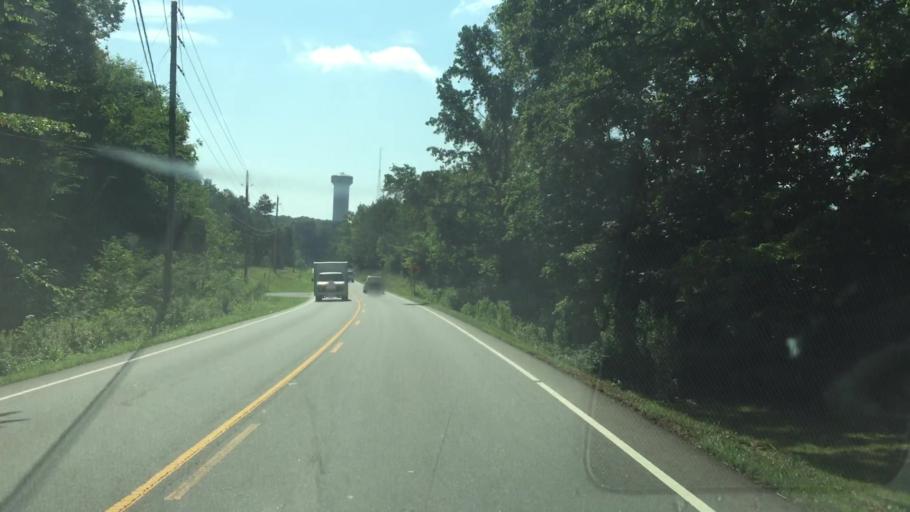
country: US
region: North Carolina
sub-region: Mecklenburg County
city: Mint Hill
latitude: 35.1660
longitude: -80.5935
